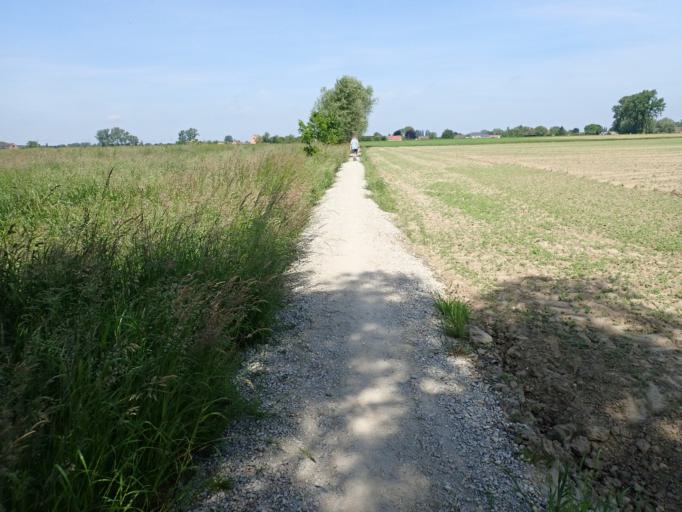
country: BE
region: Flanders
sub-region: Provincie Vlaams-Brabant
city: Kapelle-op-den-Bos
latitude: 50.9924
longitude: 4.3461
